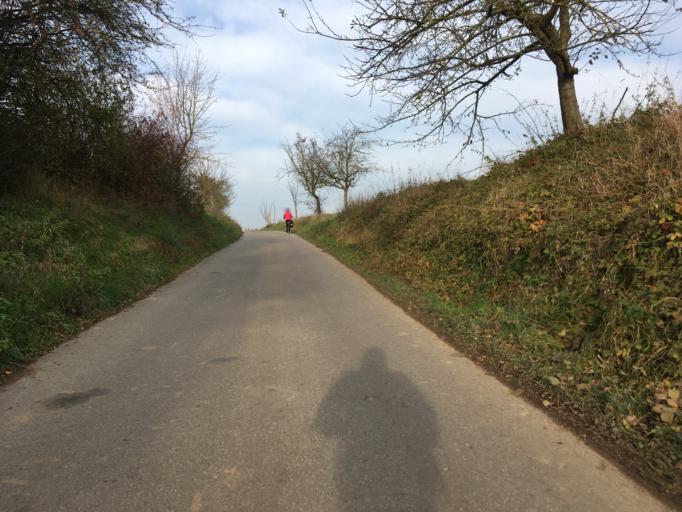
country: DE
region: Baden-Wuerttemberg
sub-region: Regierungsbezirk Stuttgart
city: Offenau
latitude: 49.2535
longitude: 9.1365
